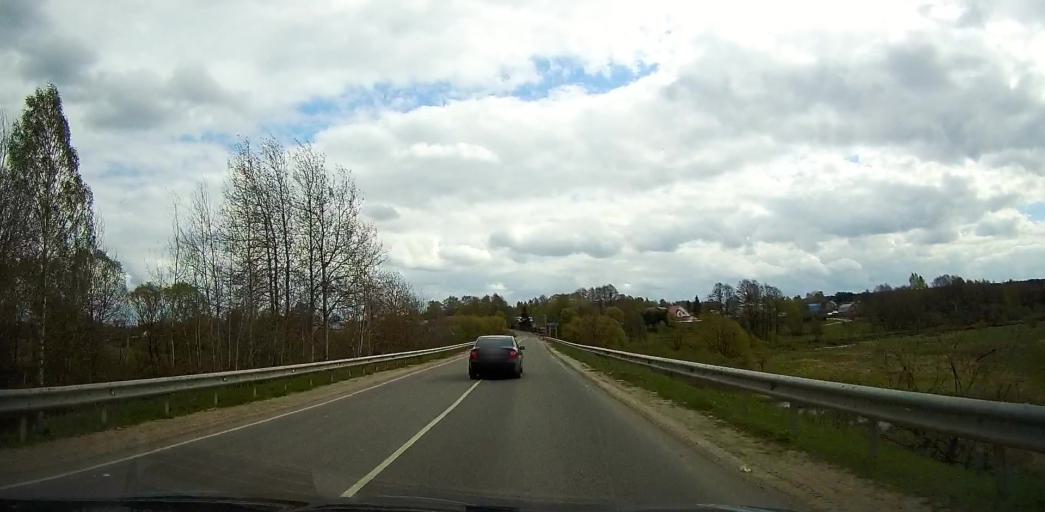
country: RU
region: Moskovskaya
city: Imeni Tsyurupy
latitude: 55.4966
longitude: 38.6284
